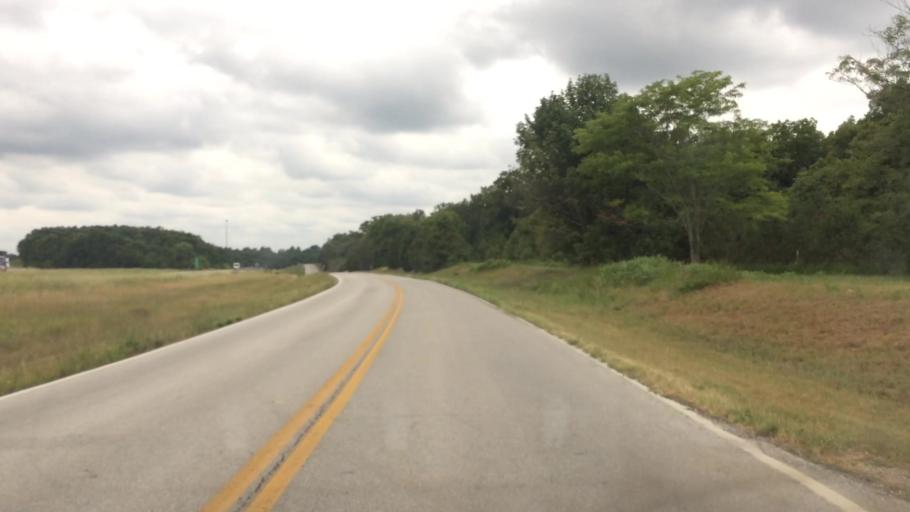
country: US
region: Missouri
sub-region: Greene County
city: Strafford
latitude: 37.2831
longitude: -93.0432
